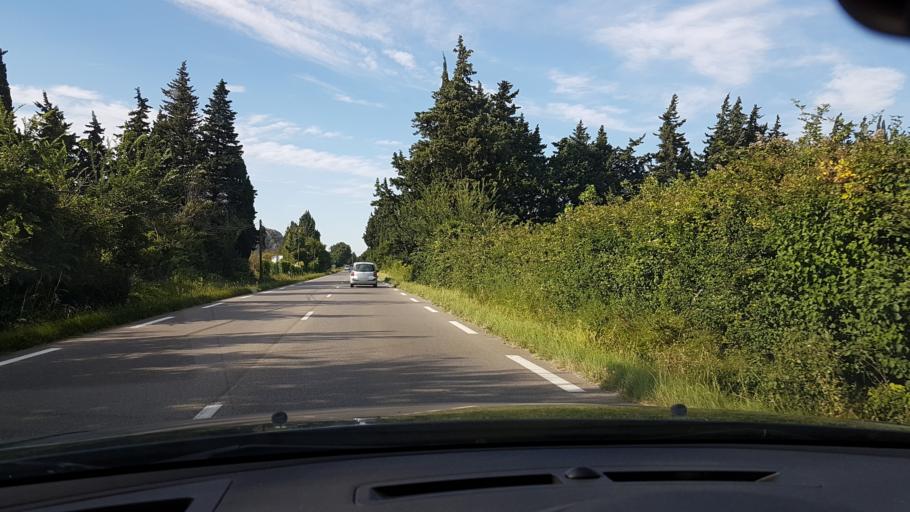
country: FR
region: Provence-Alpes-Cote d'Azur
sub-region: Departement des Bouches-du-Rhone
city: Graveson
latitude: 43.8687
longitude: 4.7708
